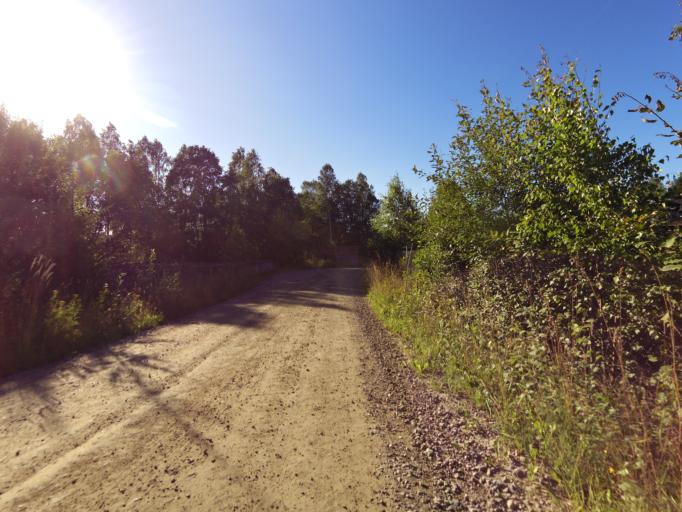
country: SE
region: Gaevleborg
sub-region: Hofors Kommun
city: Hofors
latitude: 60.5686
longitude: 16.2663
